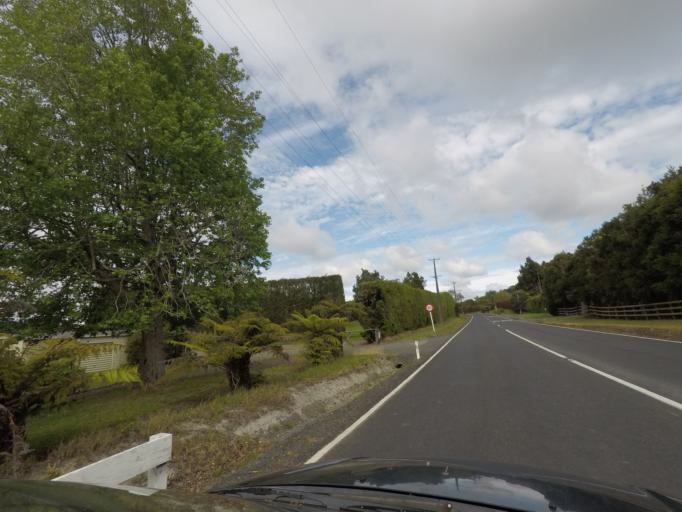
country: NZ
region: Auckland
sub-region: Auckland
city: Rosebank
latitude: -36.7749
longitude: 174.5870
